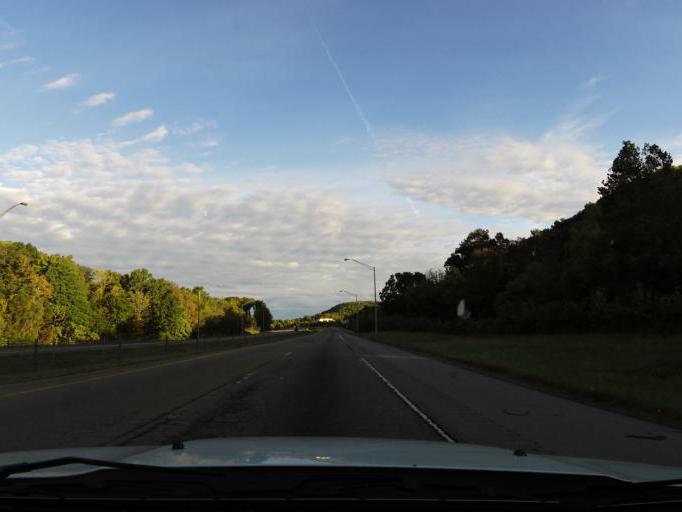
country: US
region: Tennessee
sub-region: Anderson County
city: Rocky Top
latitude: 36.2225
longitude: -84.1489
